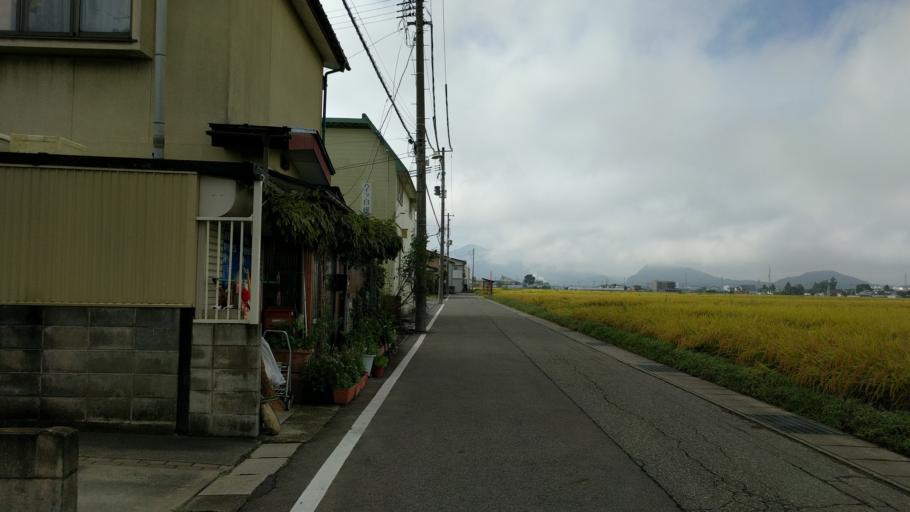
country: JP
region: Fukushima
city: Kitakata
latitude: 37.4759
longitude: 139.9220
